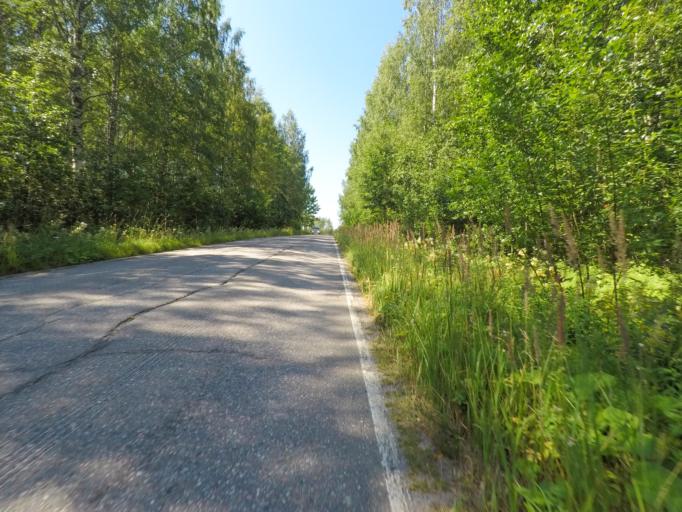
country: FI
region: Southern Savonia
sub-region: Mikkeli
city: Puumala
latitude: 61.4516
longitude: 28.1637
